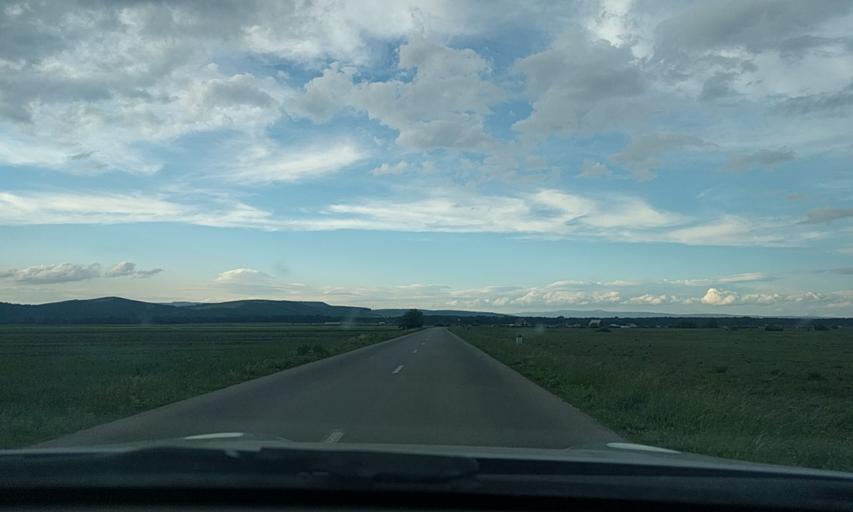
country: RO
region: Brasov
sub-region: Comuna Harman
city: Harman
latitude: 45.7293
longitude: 25.6997
